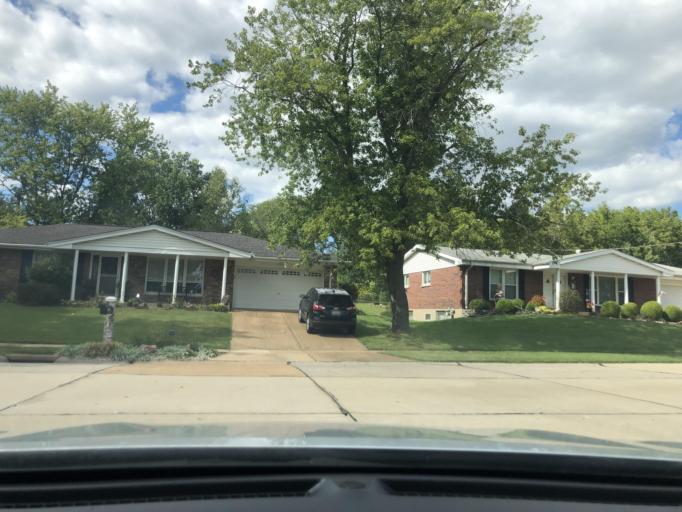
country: US
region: Missouri
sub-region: Saint Louis County
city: Concord
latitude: 38.5012
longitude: -90.3569
